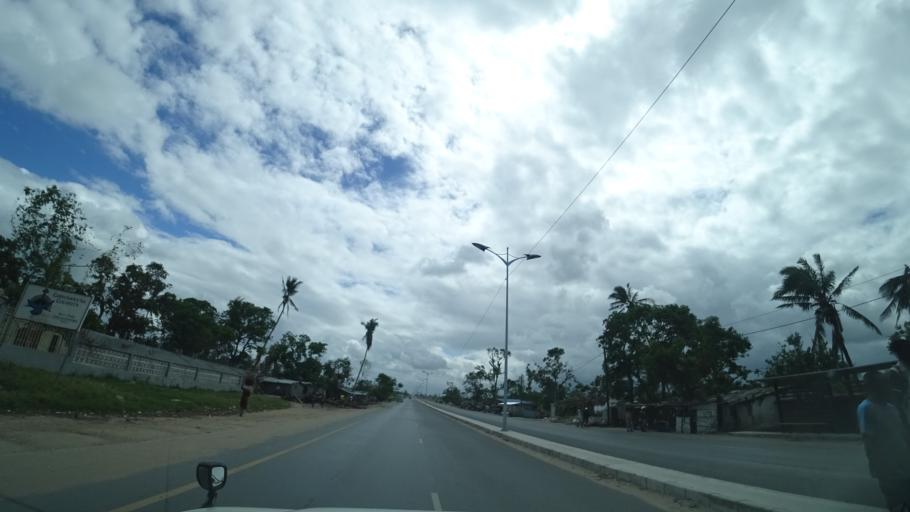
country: MZ
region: Sofala
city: Dondo
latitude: -19.6064
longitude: 34.7429
